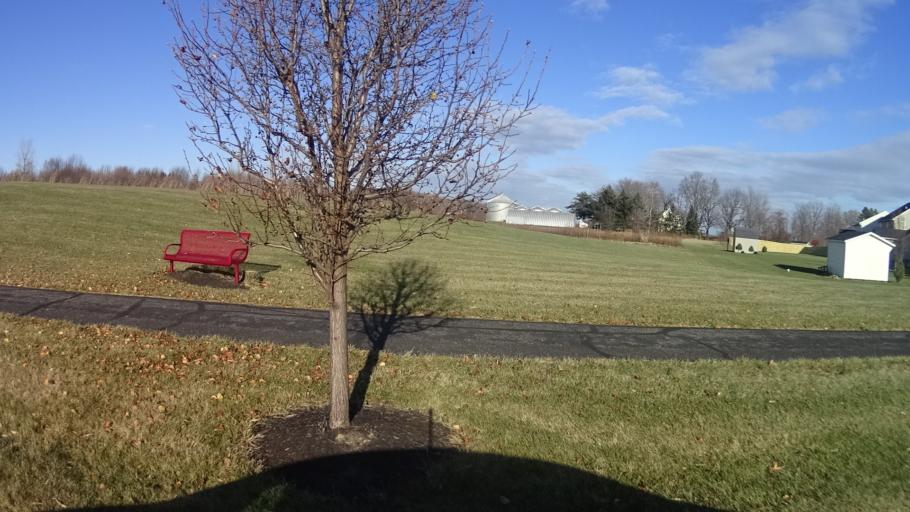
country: US
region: Ohio
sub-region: Lorain County
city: North Ridgeville
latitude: 41.4096
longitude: -82.0424
